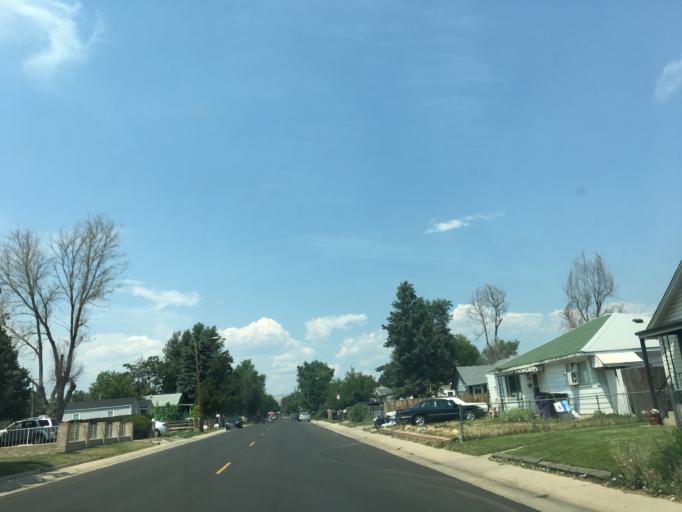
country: US
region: Colorado
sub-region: Jefferson County
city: Lakewood
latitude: 39.7040
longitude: -105.0304
